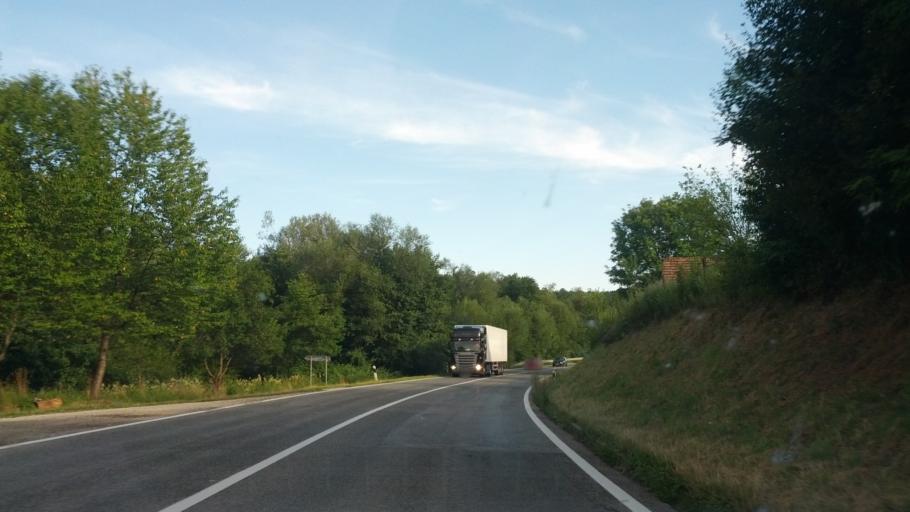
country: HR
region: Karlovacka
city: Vojnic
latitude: 45.3002
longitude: 15.6048
